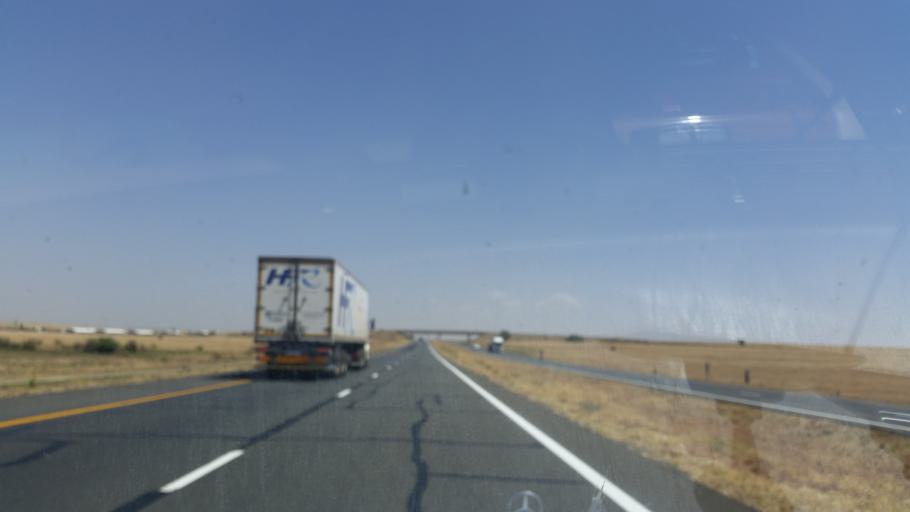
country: ZA
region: Orange Free State
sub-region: Lejweleputswa District Municipality
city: Brandfort
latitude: -28.8646
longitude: 26.5365
